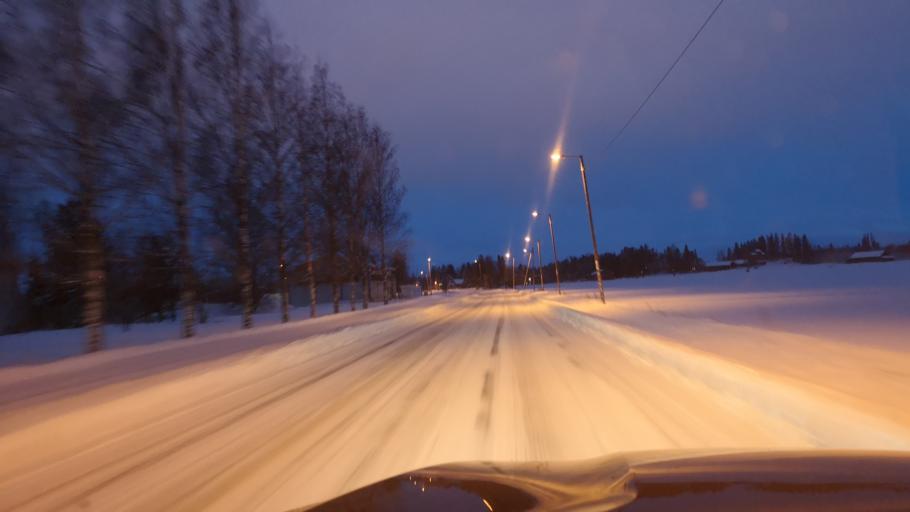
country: FI
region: Varsinais-Suomi
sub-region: Loimaa
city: Loimaa
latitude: 60.8601
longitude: 23.0717
